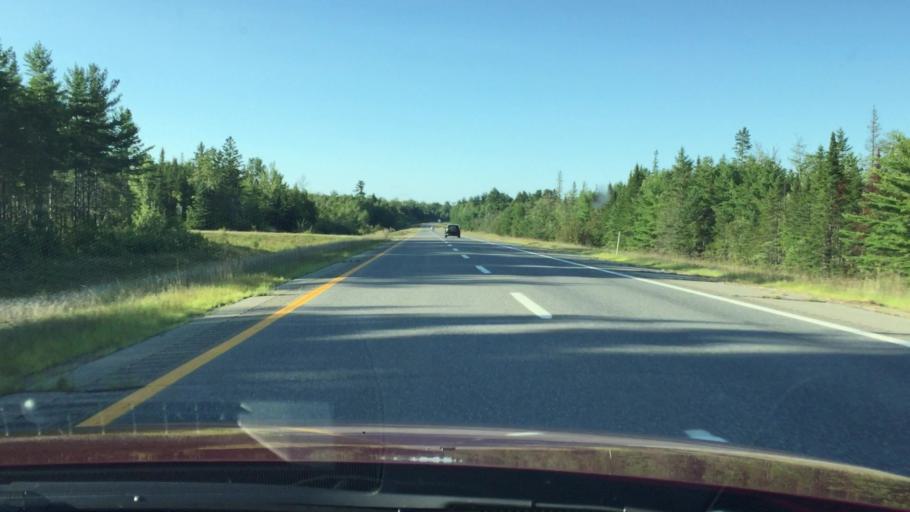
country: US
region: Maine
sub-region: Penobscot County
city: Lincoln
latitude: 45.4421
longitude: -68.5898
